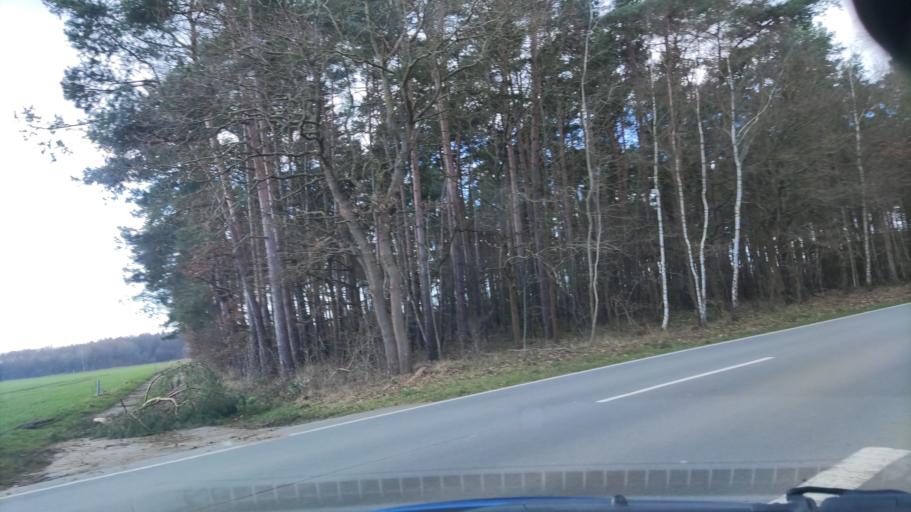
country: DE
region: Lower Saxony
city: Beedenbostel
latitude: 52.6393
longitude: 10.2092
